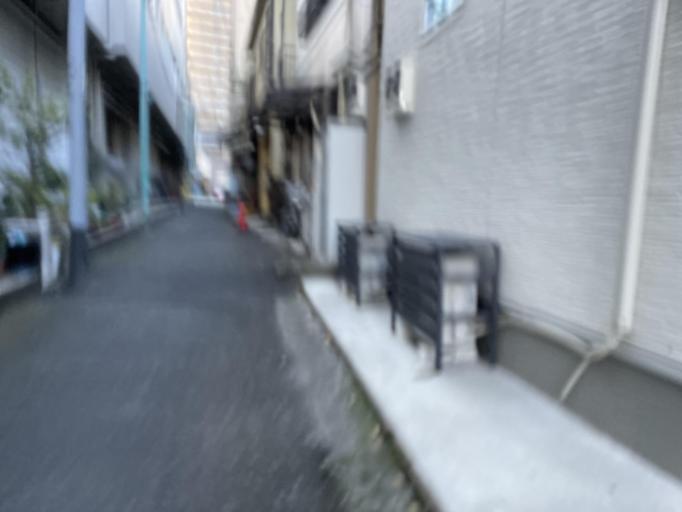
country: JP
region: Saitama
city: Soka
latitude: 35.8290
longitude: 139.8069
